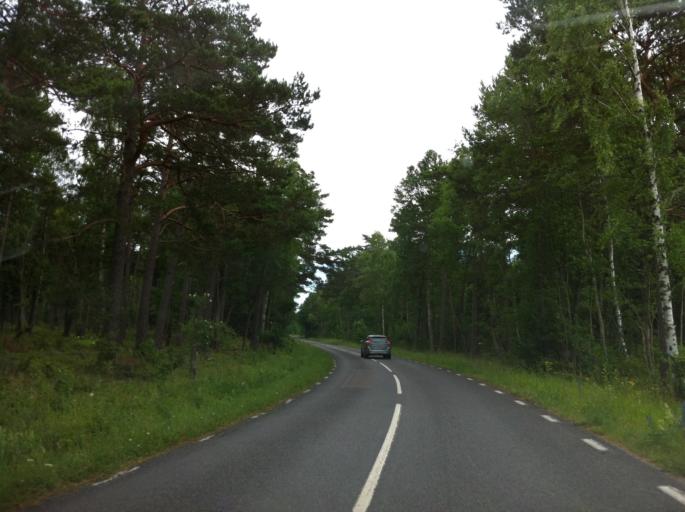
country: SE
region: Kalmar
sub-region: Vasterviks Kommun
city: Vaestervik
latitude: 57.3470
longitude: 17.0816
